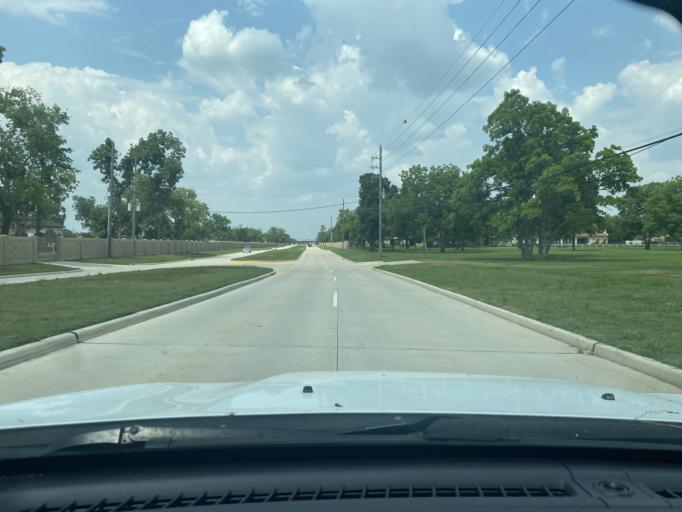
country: US
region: Texas
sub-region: Fort Bend County
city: Greatwood
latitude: 29.5464
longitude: -95.7218
